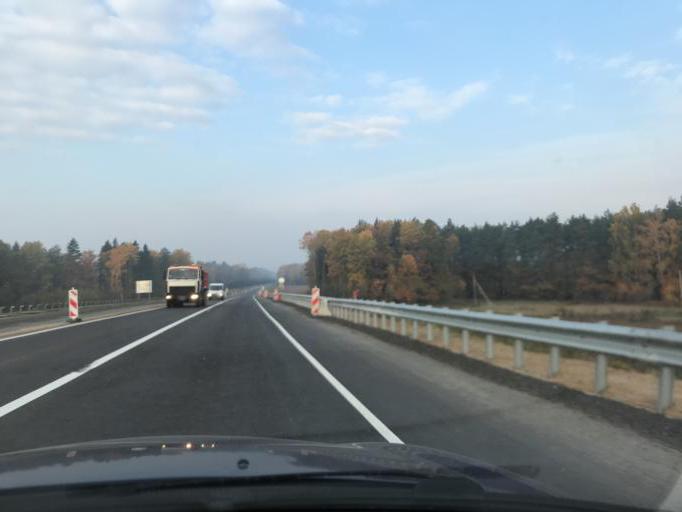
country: BY
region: Grodnenskaya
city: Lida
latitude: 53.8299
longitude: 25.3426
